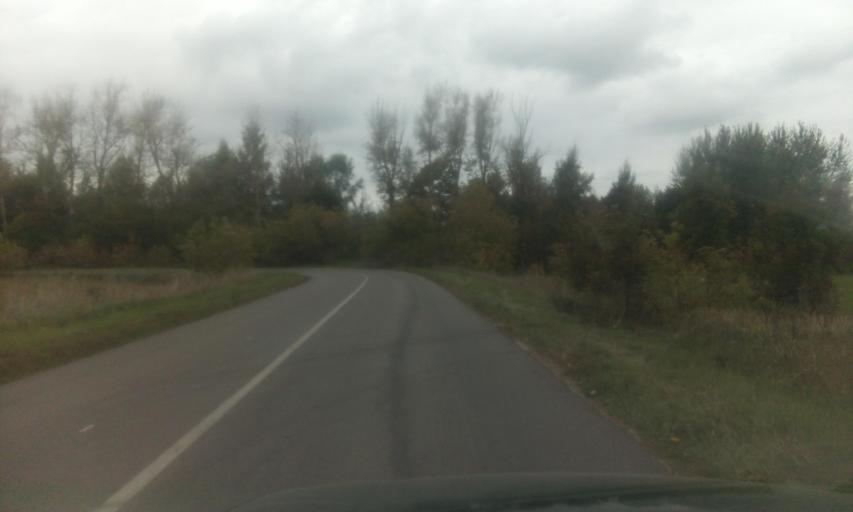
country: RU
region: Tula
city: Dubovka
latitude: 53.9575
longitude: 38.0716
